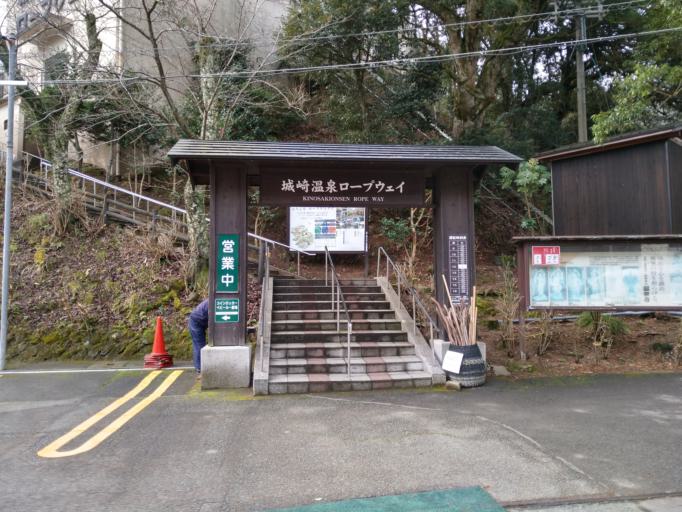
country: JP
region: Hyogo
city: Toyooka
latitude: 35.6255
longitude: 134.8040
